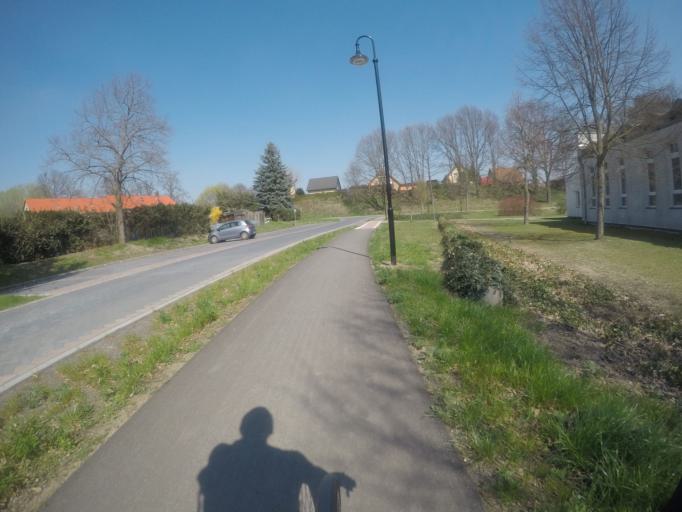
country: DE
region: Brandenburg
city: Brieselang
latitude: 52.6525
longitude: 13.0103
